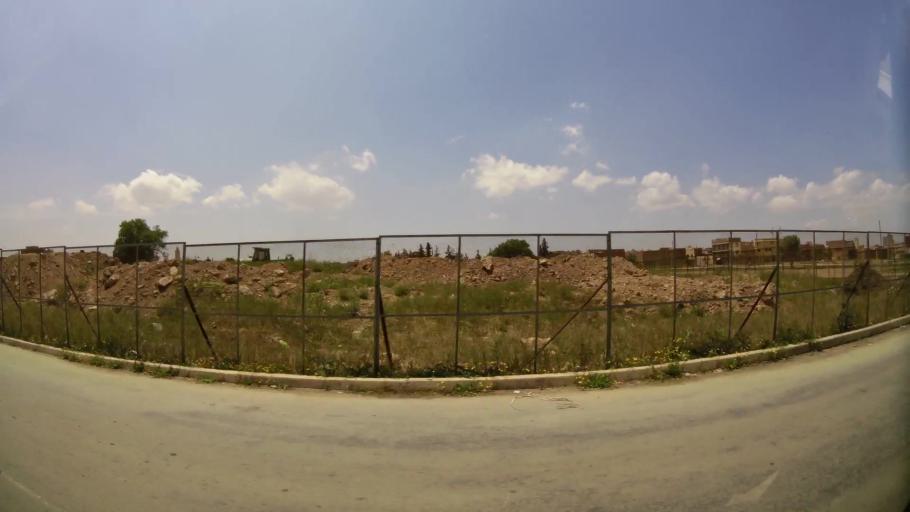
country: MA
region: Oriental
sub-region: Oujda-Angad
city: Oujda
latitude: 34.6914
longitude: -1.8991
